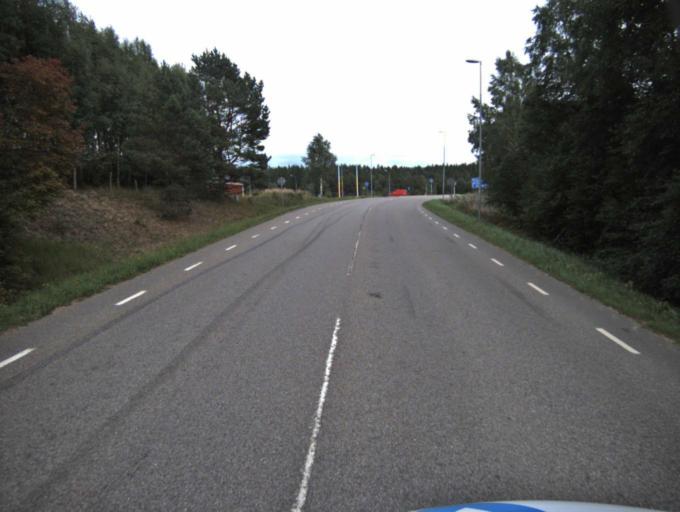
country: SE
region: Vaestra Goetaland
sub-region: Ulricehamns Kommun
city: Ulricehamn
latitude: 57.8225
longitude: 13.4265
